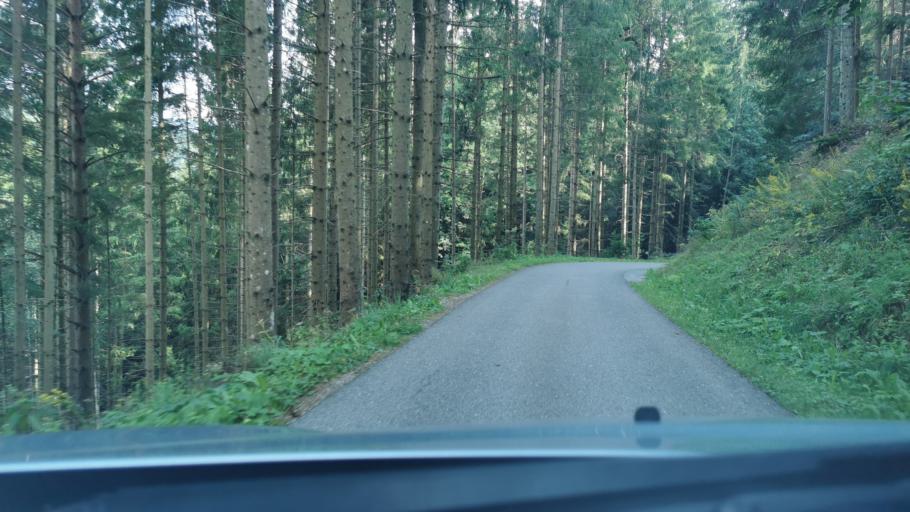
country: AT
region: Styria
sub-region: Politischer Bezirk Weiz
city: Strallegg
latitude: 47.4012
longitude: 15.6976
